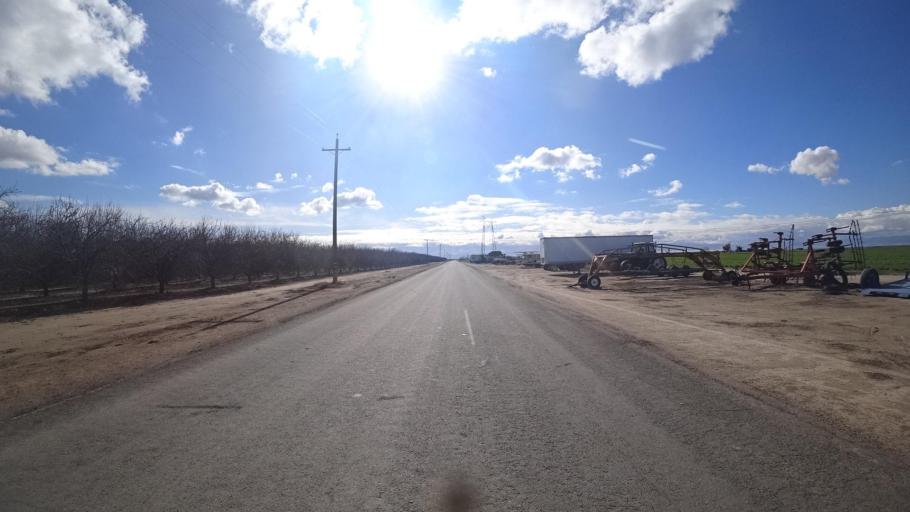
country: US
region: California
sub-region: Kern County
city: Greenfield
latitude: 35.2584
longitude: -119.1284
